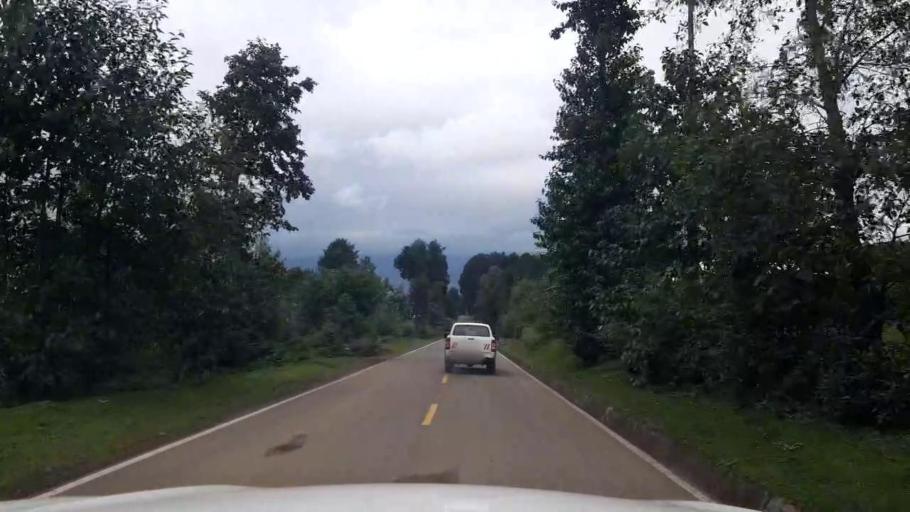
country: RW
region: Northern Province
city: Musanze
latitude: -1.4307
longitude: 29.5609
